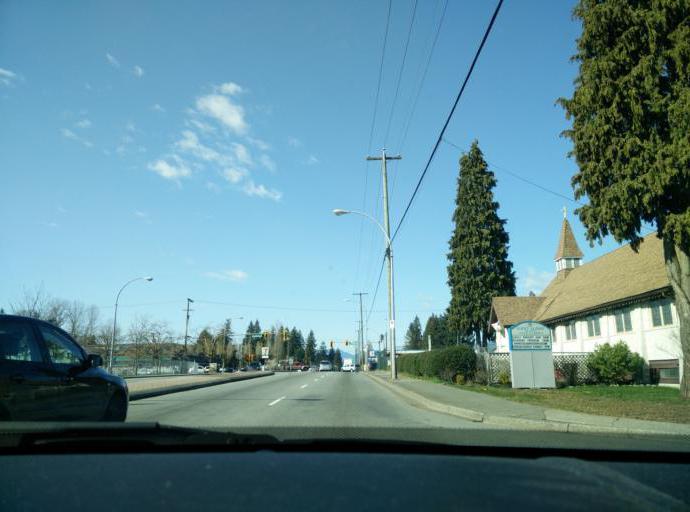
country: CA
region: British Columbia
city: New Westminster
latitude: 49.2233
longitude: -122.9399
